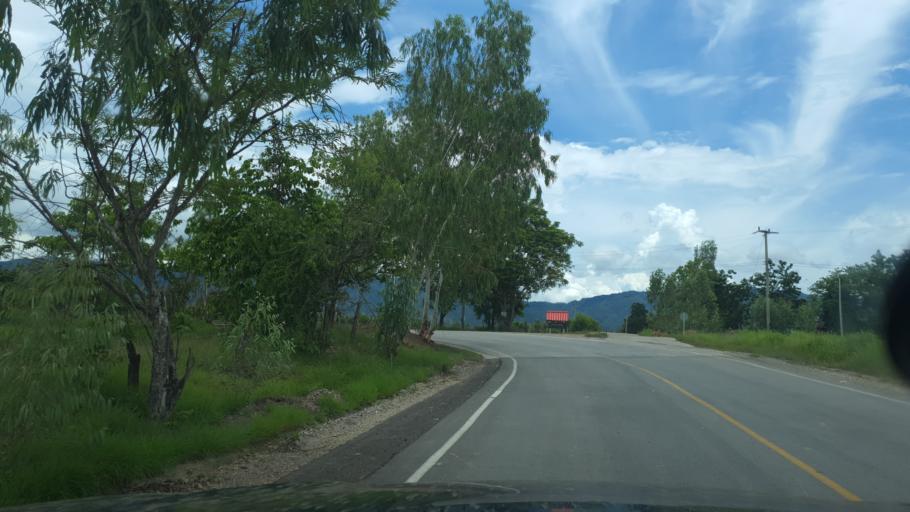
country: TH
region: Lampang
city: Sop Prap
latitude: 17.9140
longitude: 99.3890
